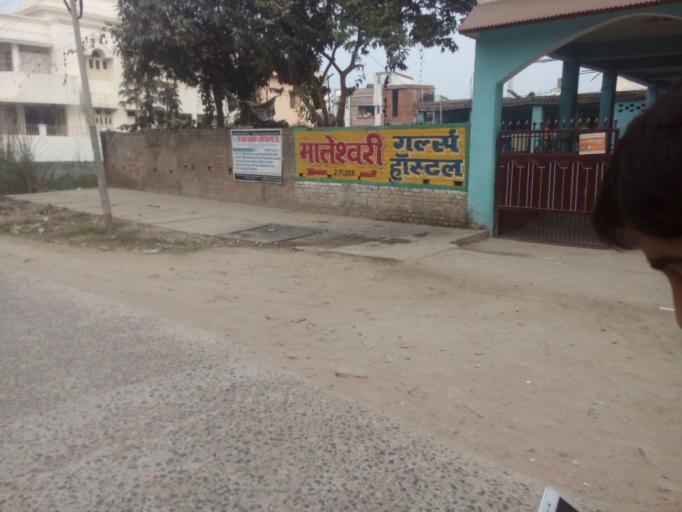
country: IN
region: Bihar
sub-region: Muzaffarpur
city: Muzaffarpur
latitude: 26.1036
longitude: 85.4022
